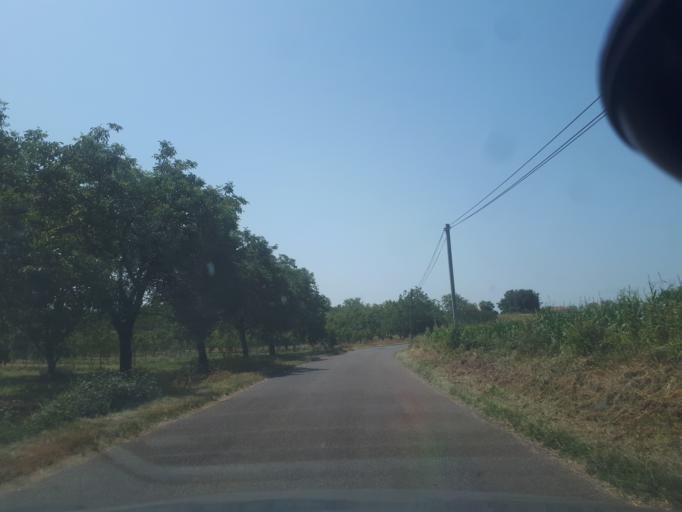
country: FR
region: Midi-Pyrenees
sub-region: Departement du Lot
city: Gourdon
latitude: 44.8263
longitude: 1.3813
